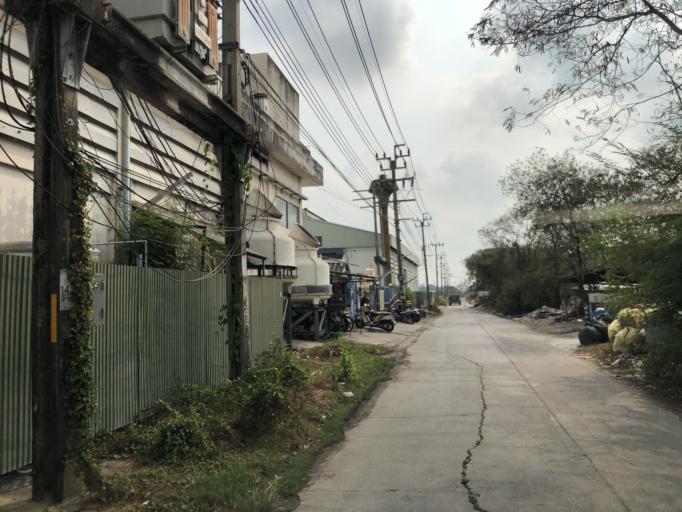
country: TH
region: Samut Prakan
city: Bang Bo District
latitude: 13.5841
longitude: 100.7107
